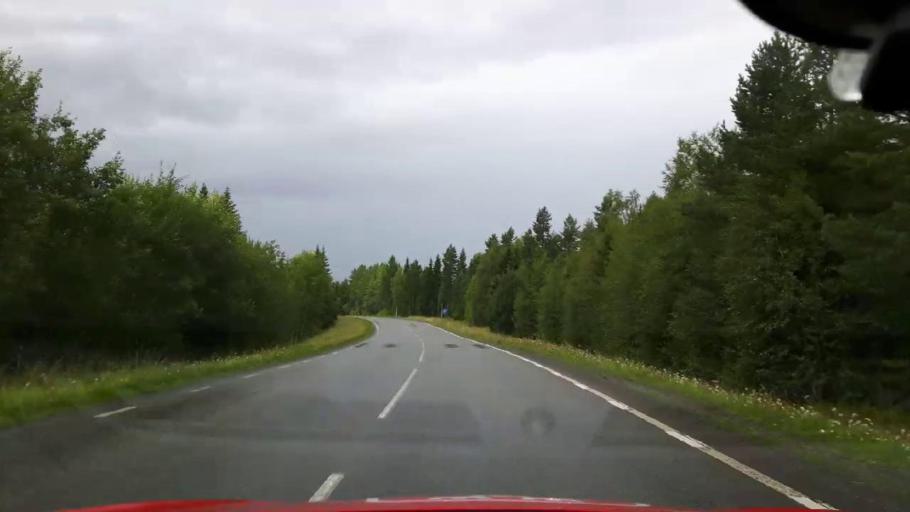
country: SE
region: Jaemtland
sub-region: Krokoms Kommun
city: Krokom
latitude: 63.3321
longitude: 14.2862
